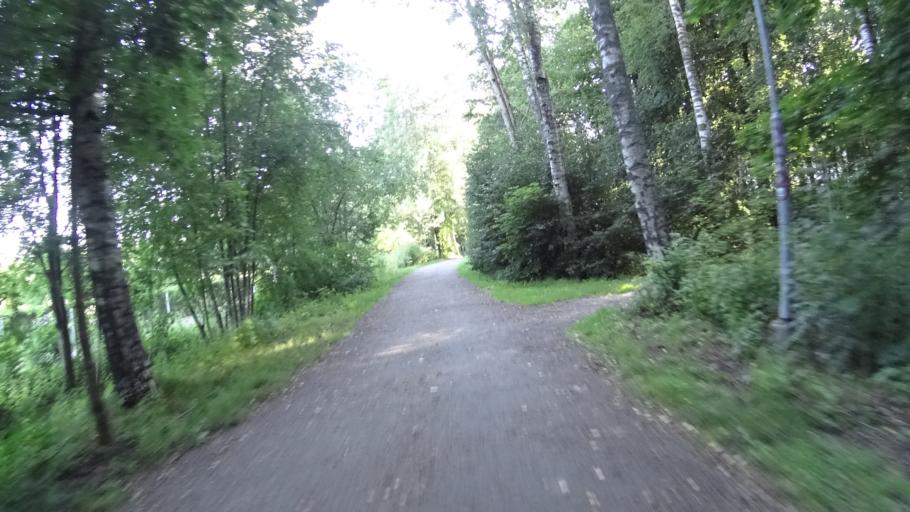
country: FI
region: Uusimaa
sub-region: Helsinki
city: Teekkarikylae
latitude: 60.2173
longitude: 24.8580
